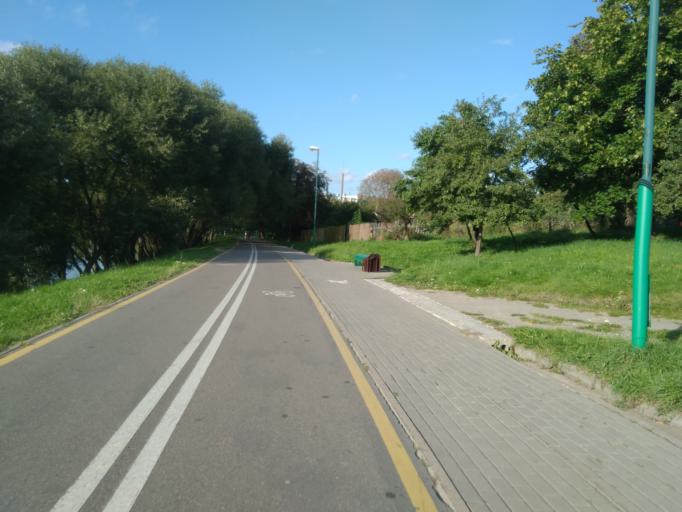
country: BY
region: Minsk
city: Minsk
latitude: 53.8790
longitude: 27.5746
